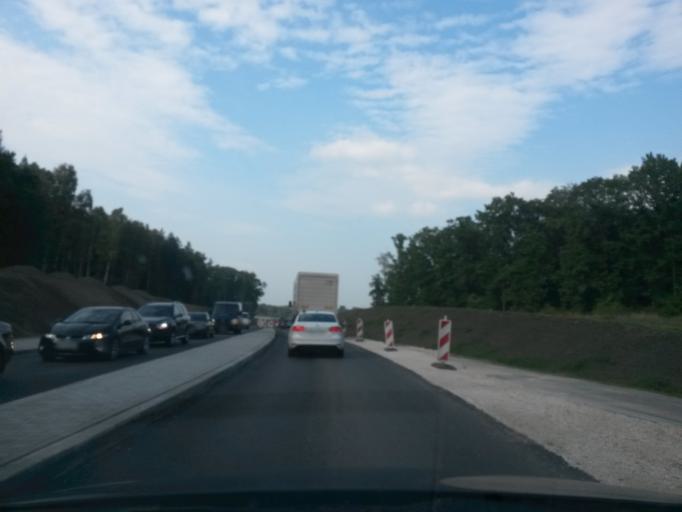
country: PL
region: Lesser Poland Voivodeship
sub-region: Powiat brzeski
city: Brzesko
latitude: 49.9847
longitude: 20.5934
